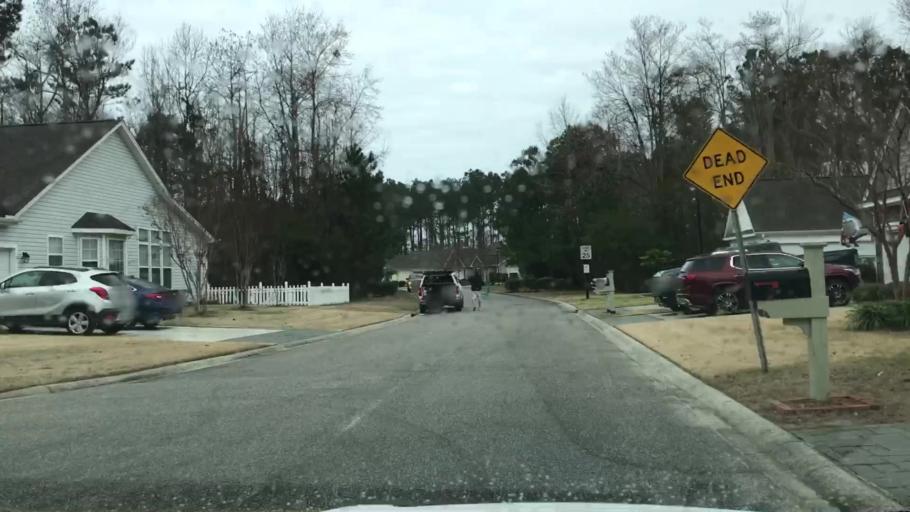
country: US
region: South Carolina
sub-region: Horry County
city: Red Hill
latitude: 33.7779
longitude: -79.0093
